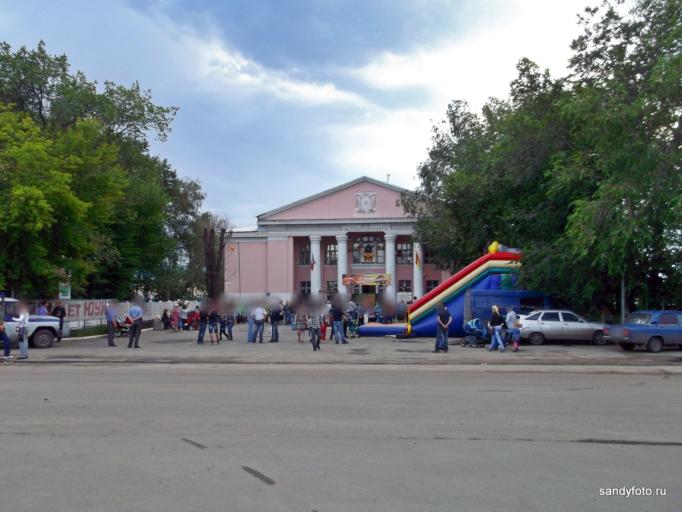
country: RU
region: Chelyabinsk
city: Troitsk
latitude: 54.1125
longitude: 61.5675
